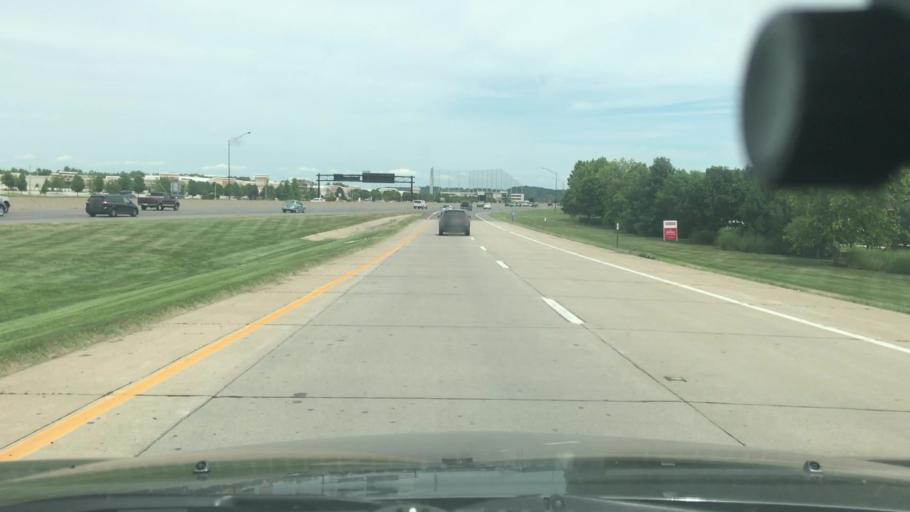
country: US
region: Missouri
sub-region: Saint Louis County
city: Chesterfield
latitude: 38.6699
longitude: -90.5971
